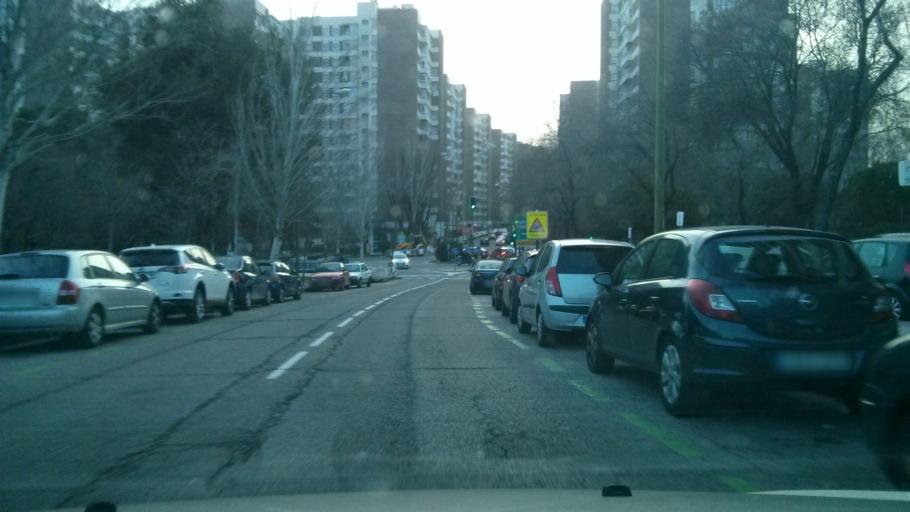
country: ES
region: Madrid
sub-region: Provincia de Madrid
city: Tetuan de las Victorias
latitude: 40.4749
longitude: -3.7015
